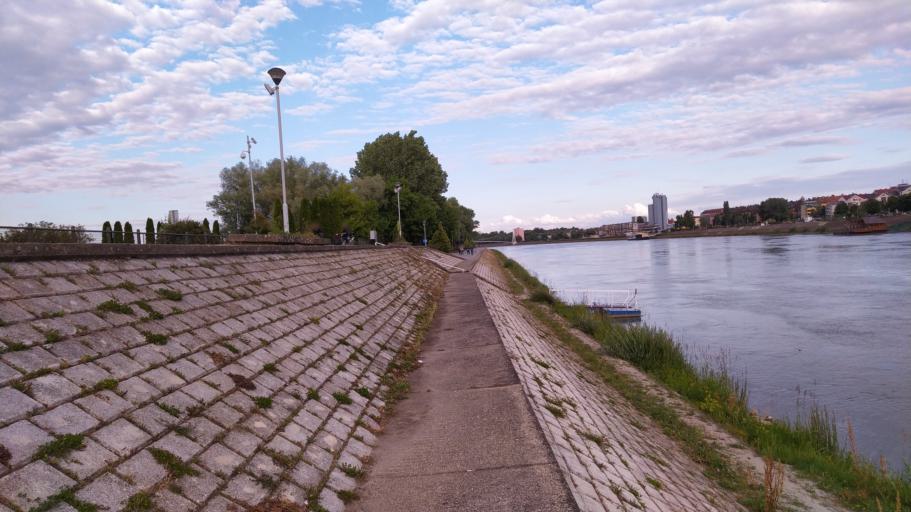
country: HR
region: Osjecko-Baranjska
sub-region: Grad Osijek
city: Osijek
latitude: 45.5679
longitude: 18.6686
